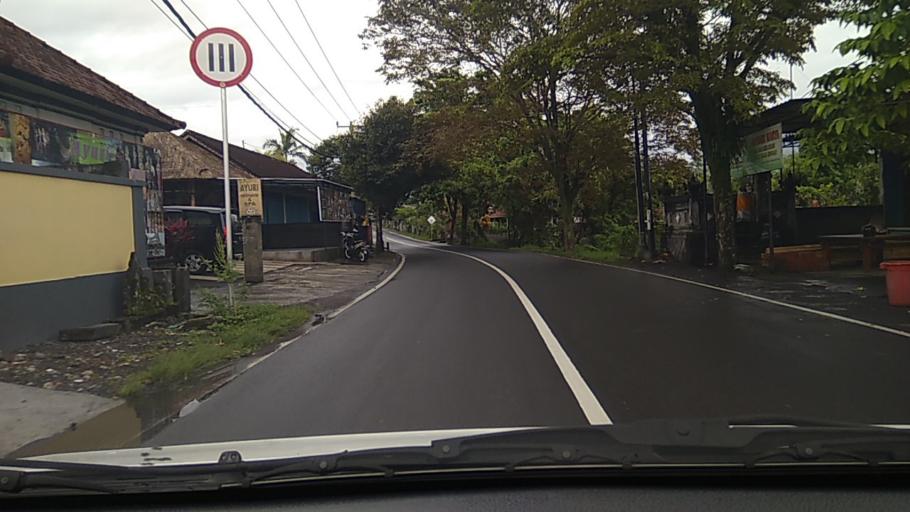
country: ID
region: Bali
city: Banjar Budakeling
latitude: -8.4330
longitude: 115.5908
